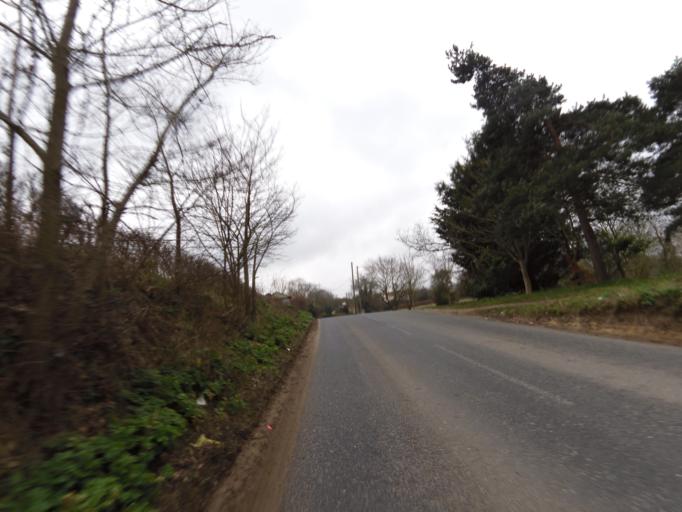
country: GB
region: England
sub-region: Suffolk
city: Wickham Market
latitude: 52.1553
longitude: 1.3883
